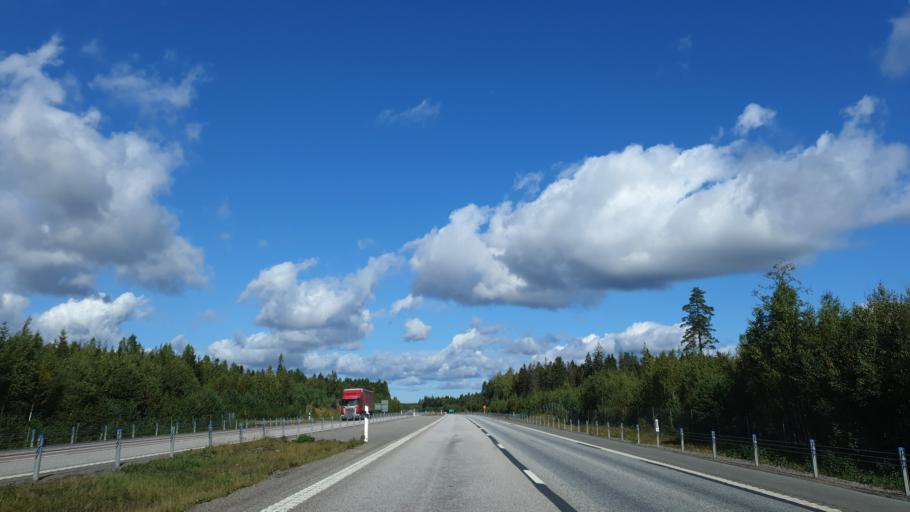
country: SE
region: Uppsala
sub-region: Tierps Kommun
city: Tierp
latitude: 60.2244
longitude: 17.4988
